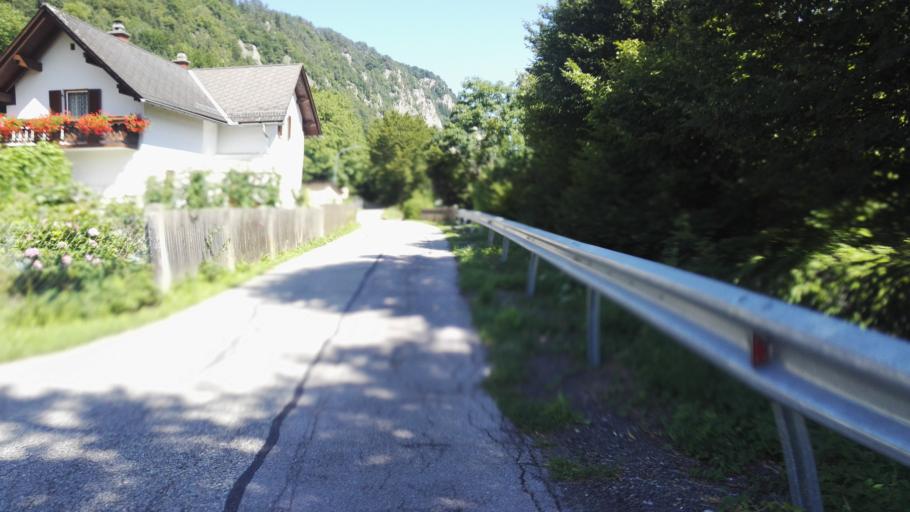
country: AT
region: Styria
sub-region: Politischer Bezirk Graz-Umgebung
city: Peggau
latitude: 47.2059
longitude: 15.3364
